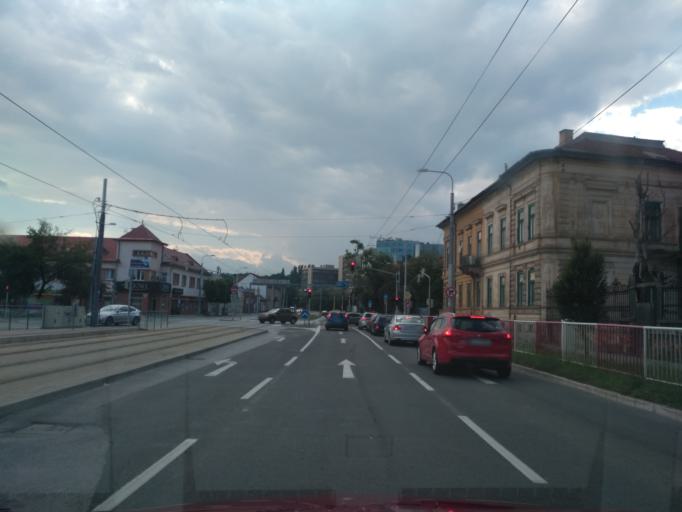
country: SK
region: Kosicky
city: Kosice
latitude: 48.7233
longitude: 21.2889
